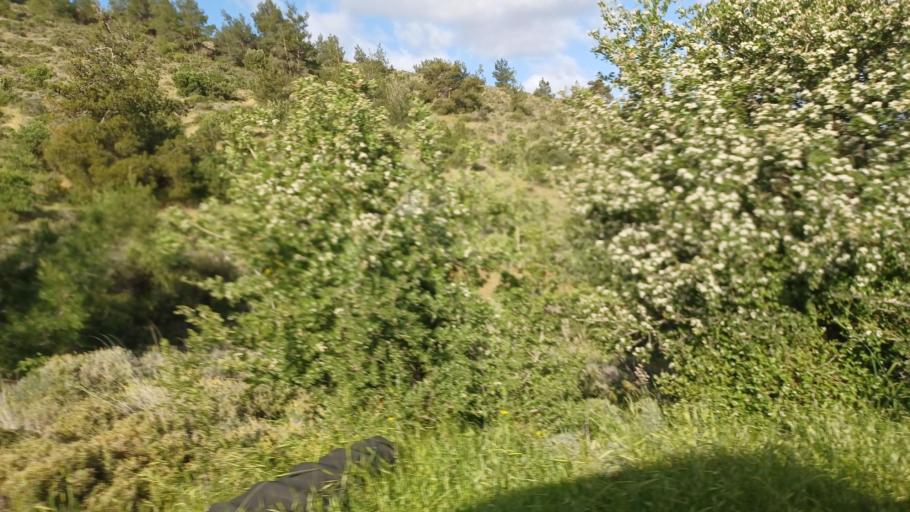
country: CY
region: Lefkosia
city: Peristerona
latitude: 35.0660
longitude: 33.0490
